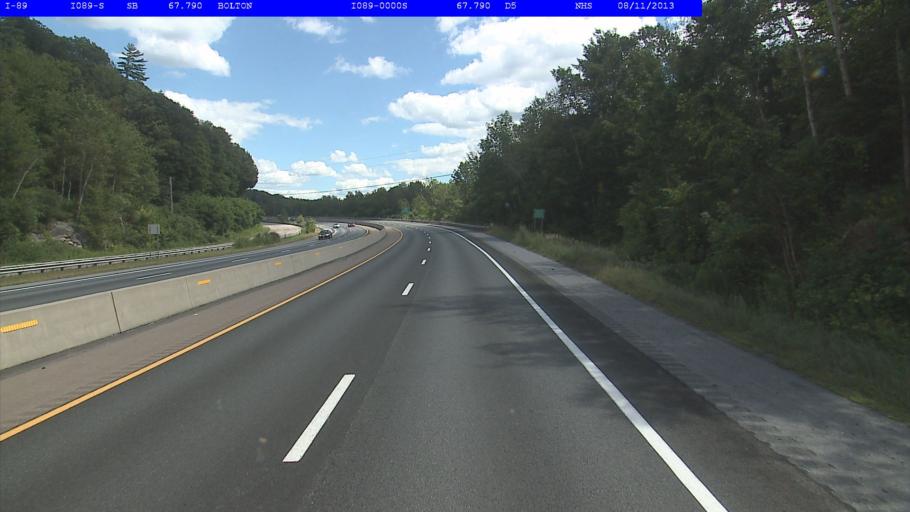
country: US
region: Vermont
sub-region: Washington County
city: Waterbury
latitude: 44.3601
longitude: -72.8257
